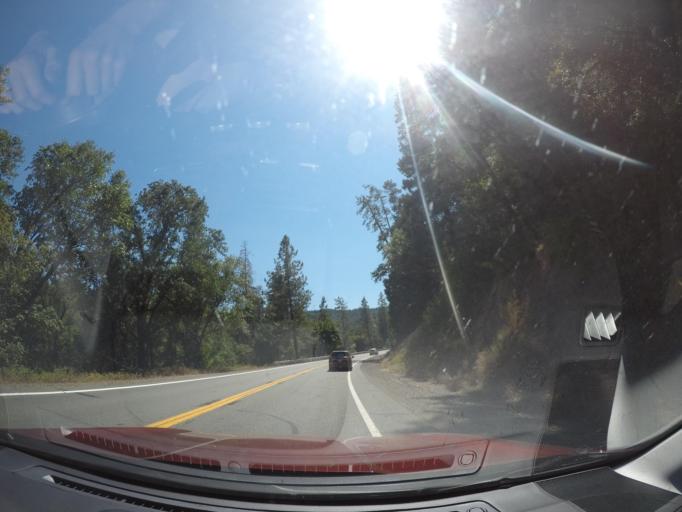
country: US
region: California
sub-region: Shasta County
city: Bella Vista
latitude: 40.7557
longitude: -122.0188
